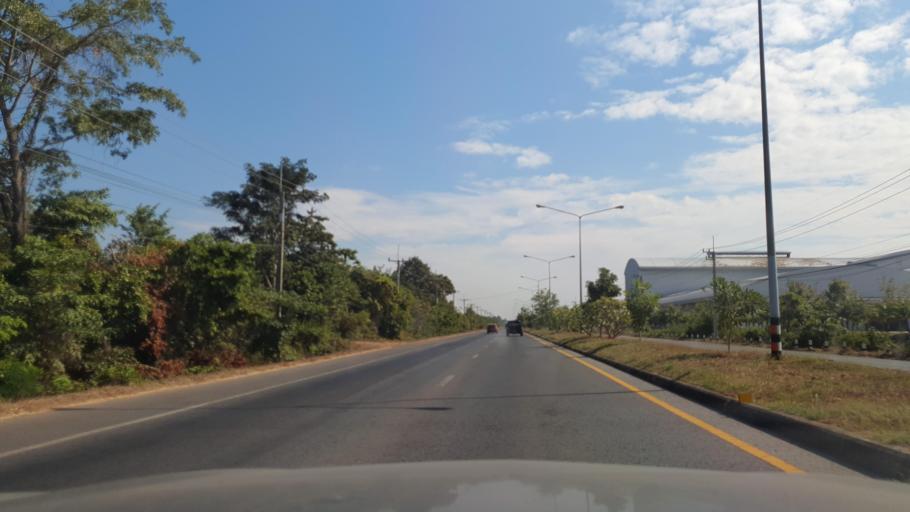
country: TH
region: Maha Sarakham
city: Kantharawichai
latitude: 16.3834
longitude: 103.2214
